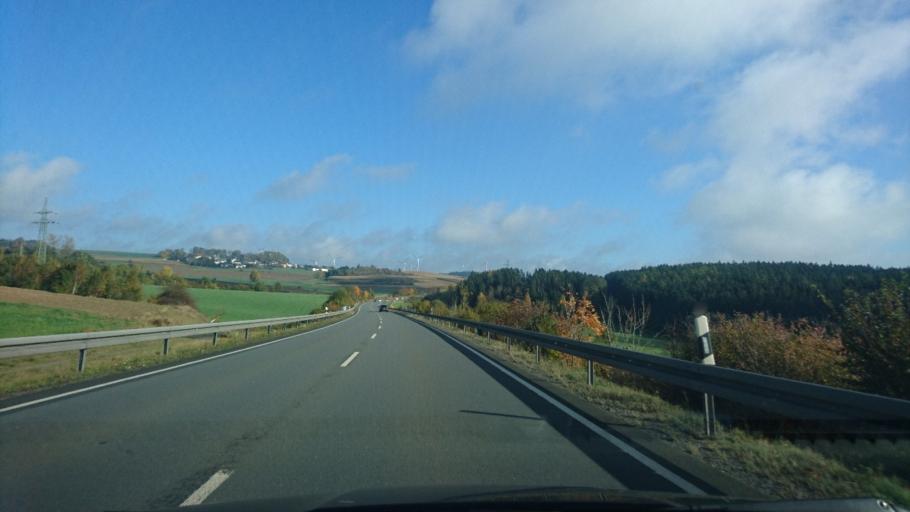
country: DE
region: Bavaria
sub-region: Upper Franconia
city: Selbitz
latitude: 50.3291
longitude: 11.7514
